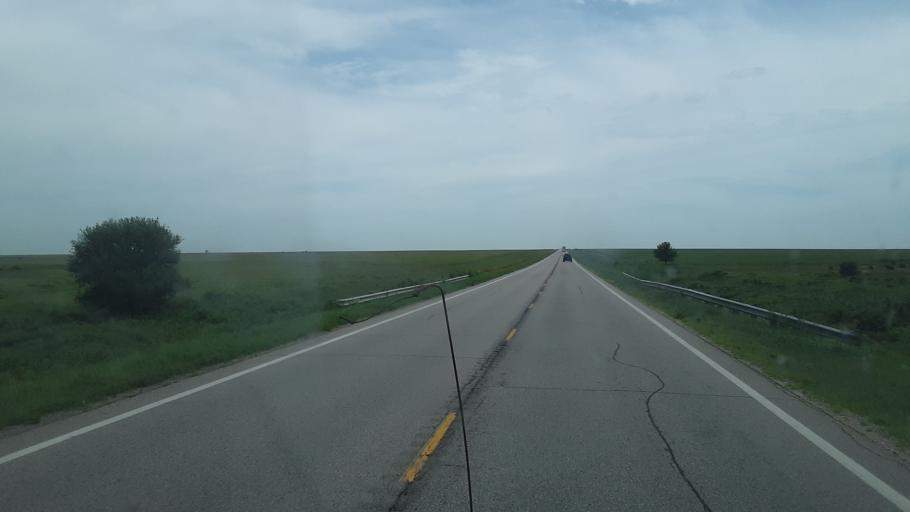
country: US
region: Kansas
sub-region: Butler County
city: El Dorado
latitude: 37.8102
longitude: -96.5978
